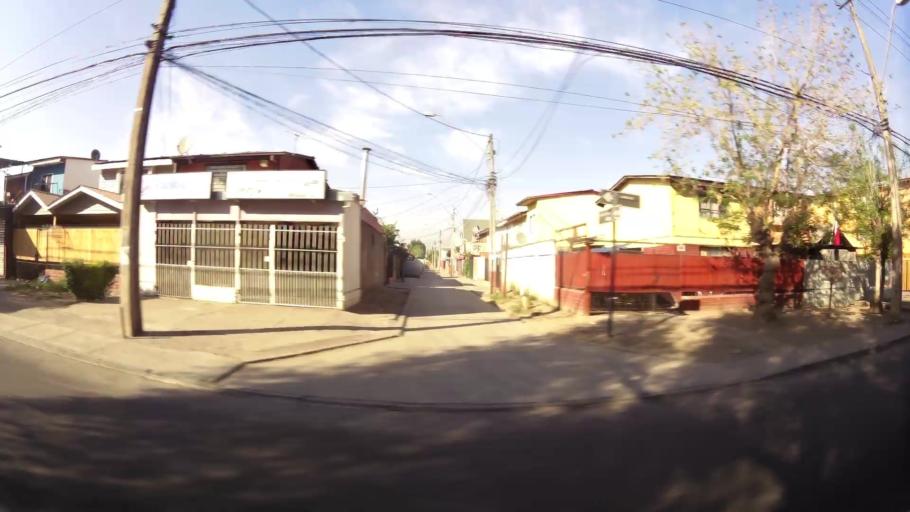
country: CL
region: Santiago Metropolitan
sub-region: Provincia de Santiago
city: Lo Prado
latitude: -33.4591
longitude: -70.7577
